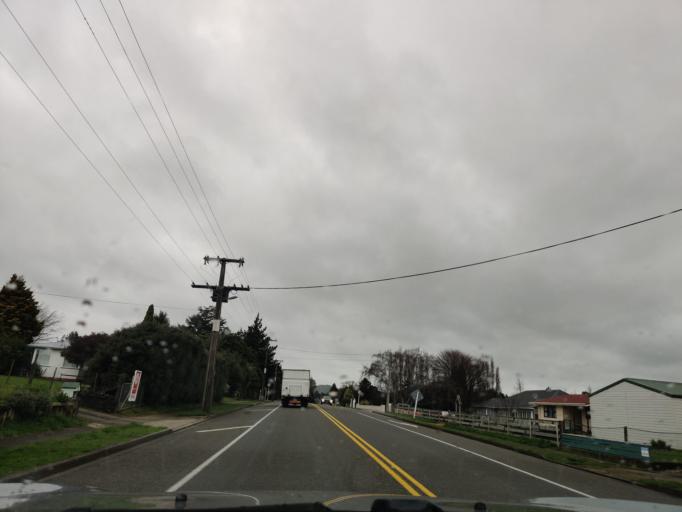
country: NZ
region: Manawatu-Wanganui
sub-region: Palmerston North City
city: Palmerston North
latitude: -40.3390
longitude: 175.8743
